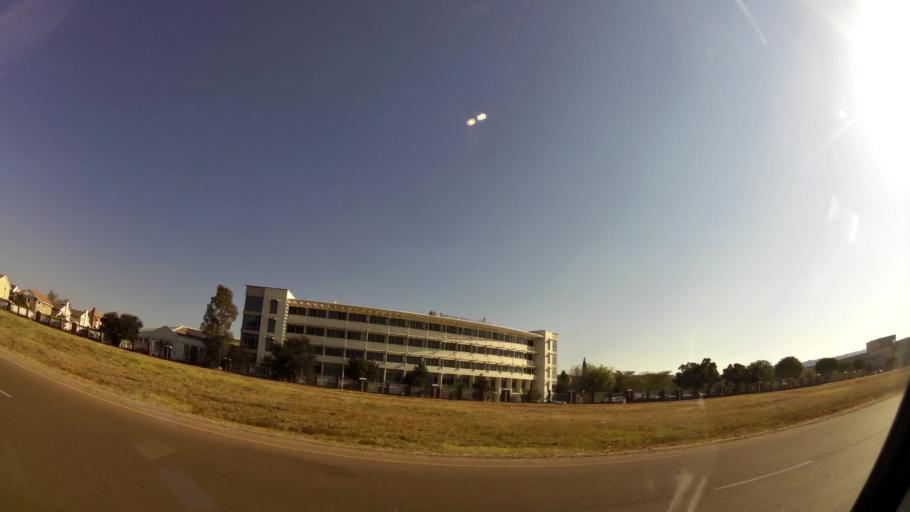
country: ZA
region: Gauteng
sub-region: City of Tshwane Metropolitan Municipality
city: Centurion
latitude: -25.8199
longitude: 28.3061
